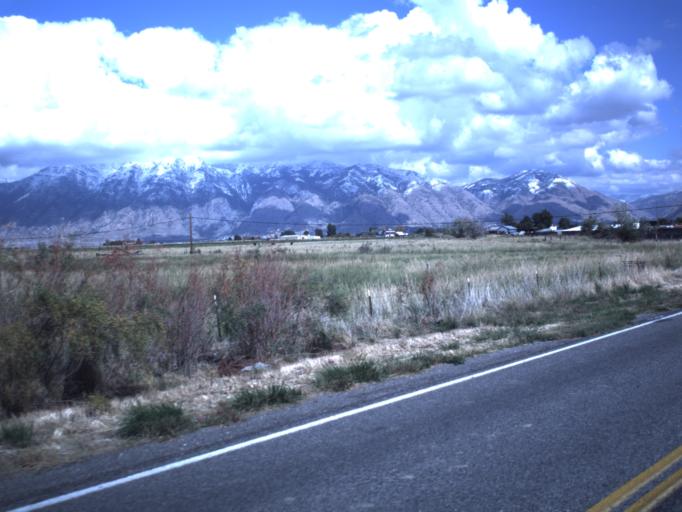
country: US
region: Utah
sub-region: Utah County
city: Spanish Fork
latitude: 40.1155
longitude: -111.6870
